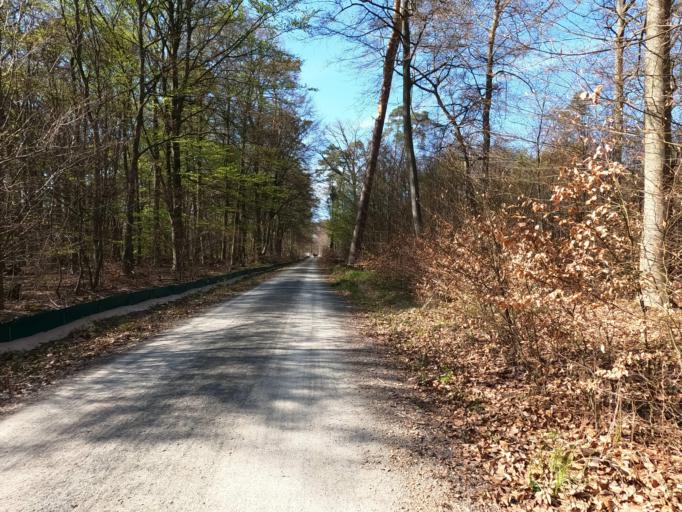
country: DE
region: Hesse
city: Langen
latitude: 50.0094
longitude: 8.6344
